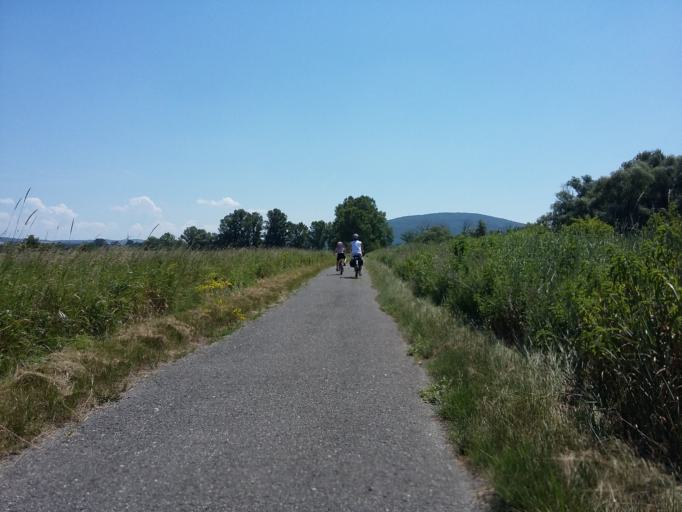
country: AT
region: Lower Austria
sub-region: Politischer Bezirk Ganserndorf
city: Marchegg
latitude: 48.2327
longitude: 16.9510
